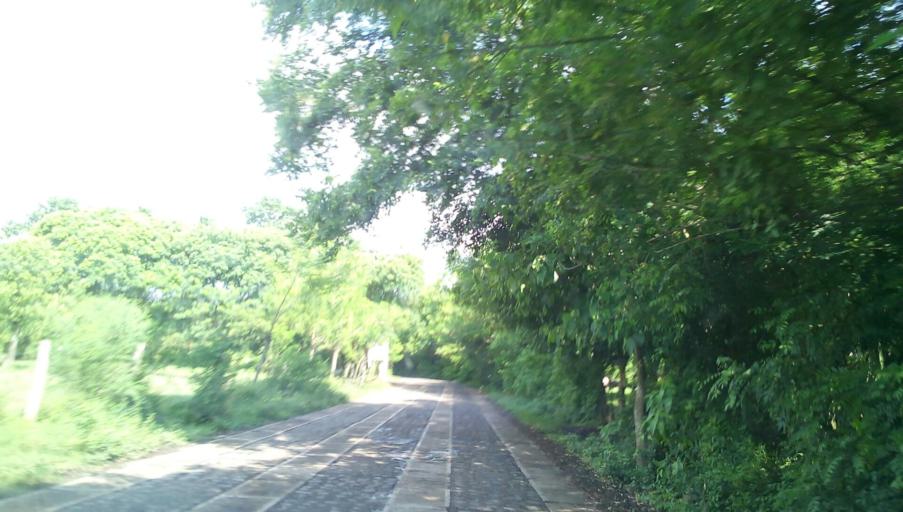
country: MX
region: Veracruz
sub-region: Citlaltepetl
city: Las Sabinas
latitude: 21.3495
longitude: -97.8944
